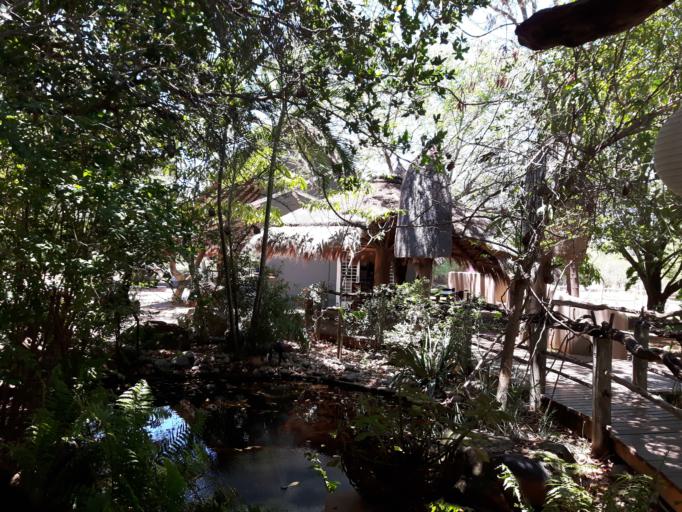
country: ZA
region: Limpopo
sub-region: Mopani District Municipality
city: Hoedspruit
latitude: -24.3746
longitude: 30.7044
